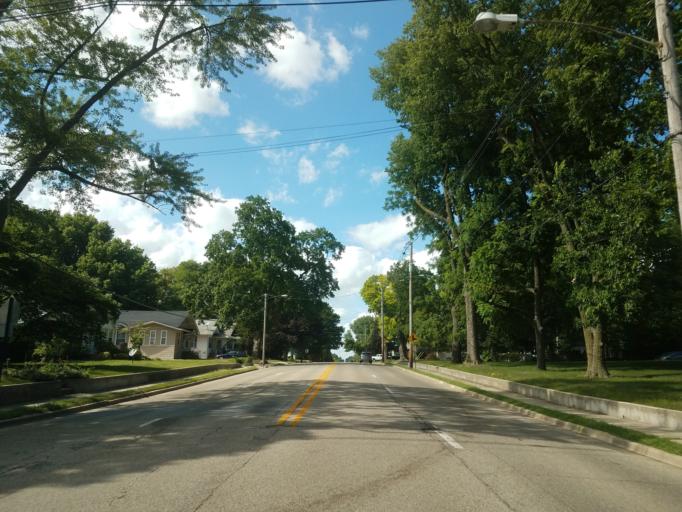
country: US
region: Illinois
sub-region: McLean County
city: Normal
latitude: 40.4983
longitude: -88.9821
